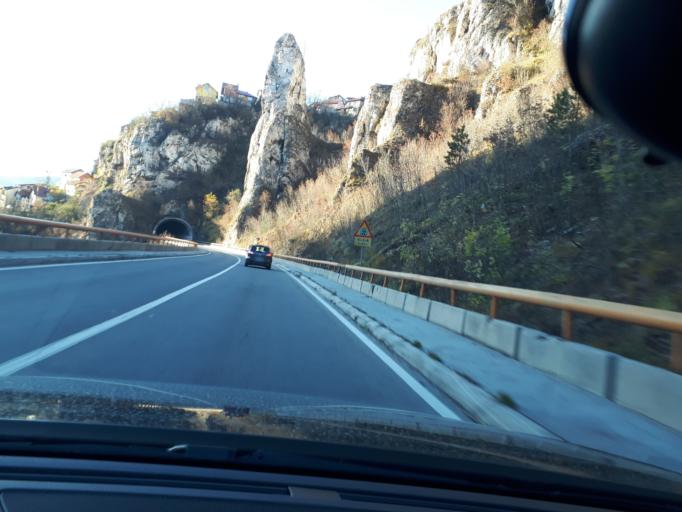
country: BA
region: Federation of Bosnia and Herzegovina
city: Kobilja Glava
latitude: 43.8580
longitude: 18.4443
